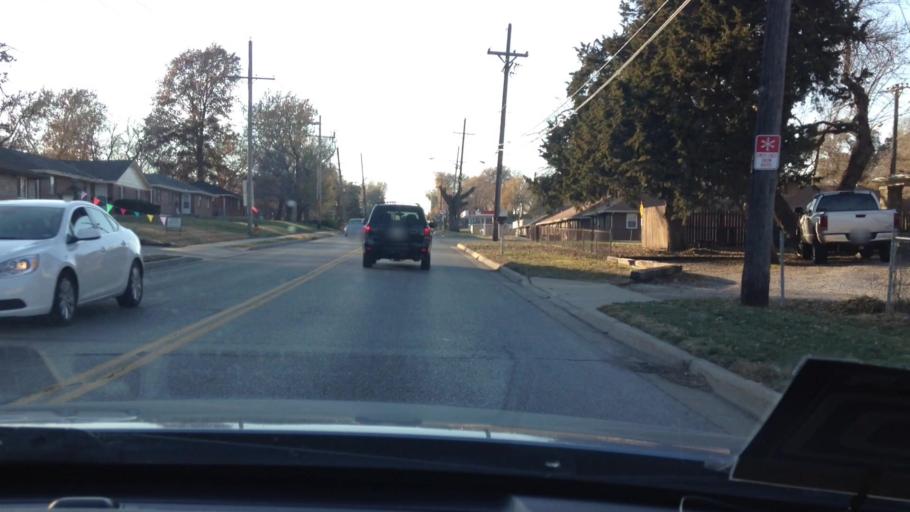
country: US
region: Kansas
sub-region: Johnson County
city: Roeland Park
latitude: 39.0441
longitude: -94.6265
